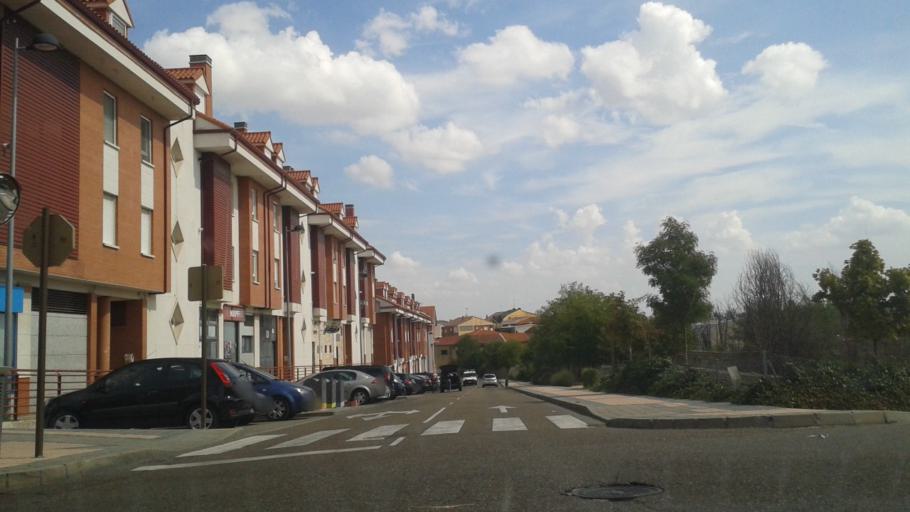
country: ES
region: Castille and Leon
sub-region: Provincia de Valladolid
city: Arroyo
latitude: 41.6248
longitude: -4.7738
